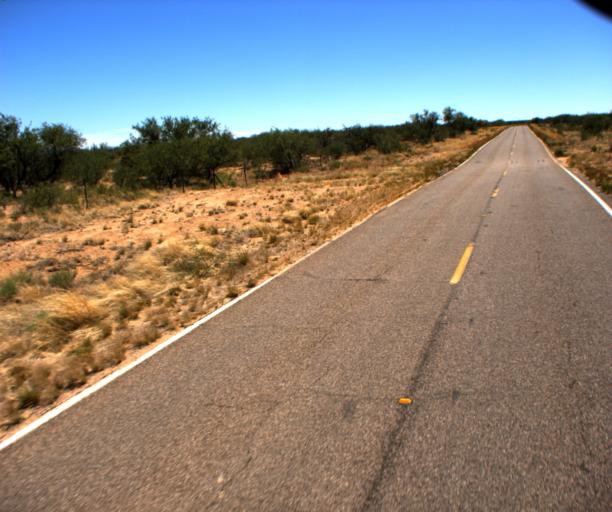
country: US
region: Arizona
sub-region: Pima County
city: Three Points
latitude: 31.8147
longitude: -111.4417
